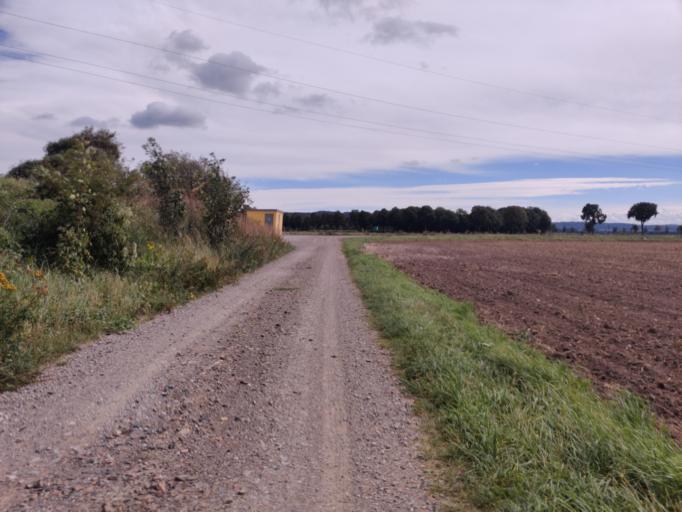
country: DE
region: Lower Saxony
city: Alt Wallmoden
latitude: 52.0250
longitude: 10.3291
